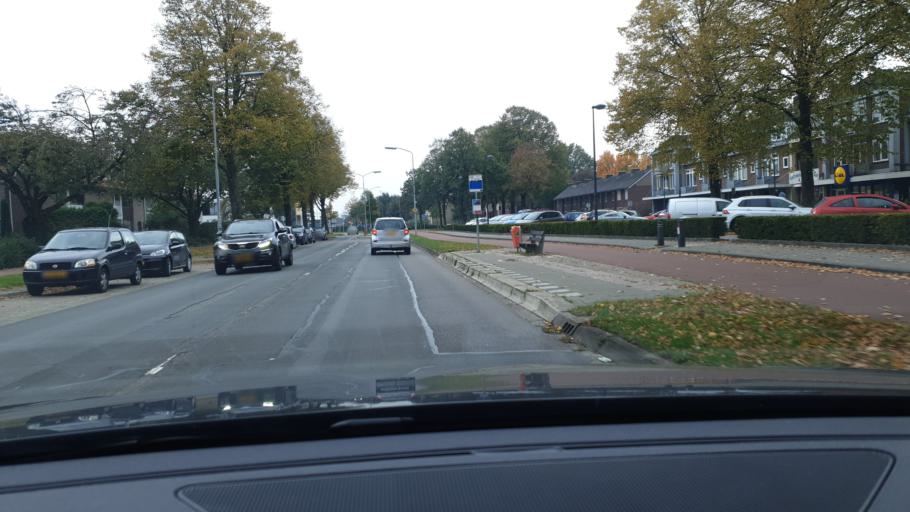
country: NL
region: North Brabant
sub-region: Gemeente Veldhoven
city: Veldhoven
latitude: 51.4135
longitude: 5.4082
